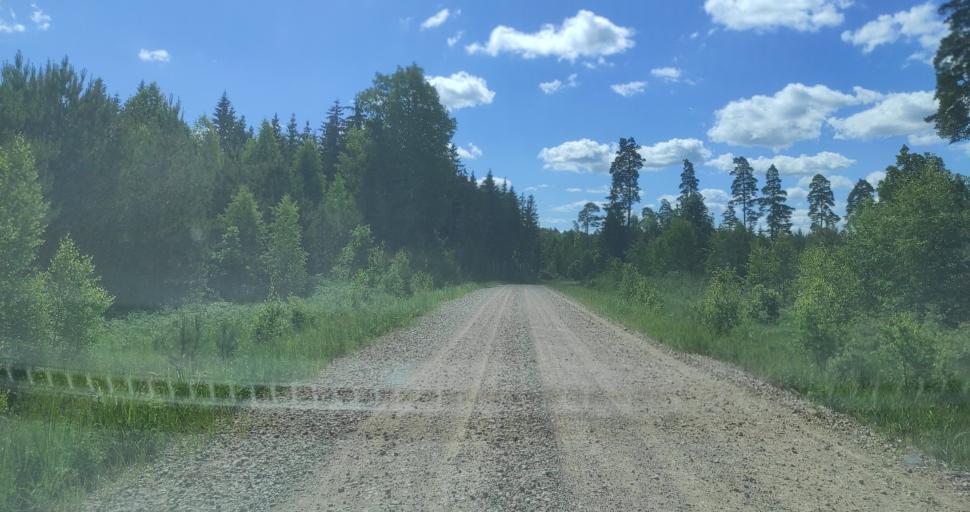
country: LV
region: Kuldigas Rajons
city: Kuldiga
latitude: 56.9469
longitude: 21.7879
